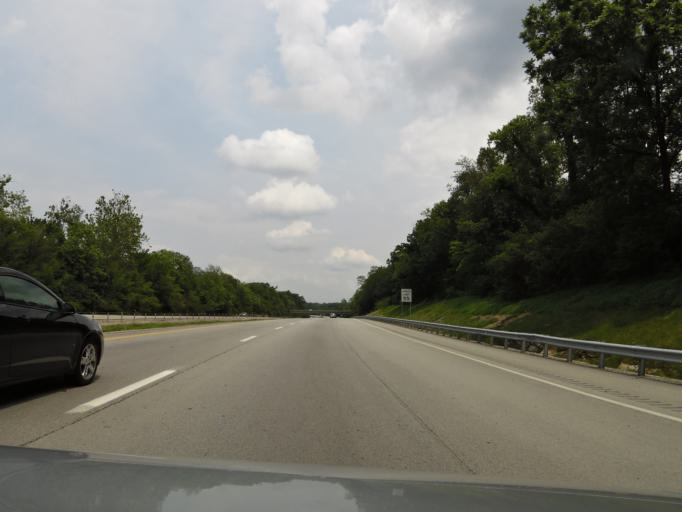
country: US
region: Kentucky
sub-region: Jefferson County
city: Northfield
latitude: 38.2926
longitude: -85.6380
